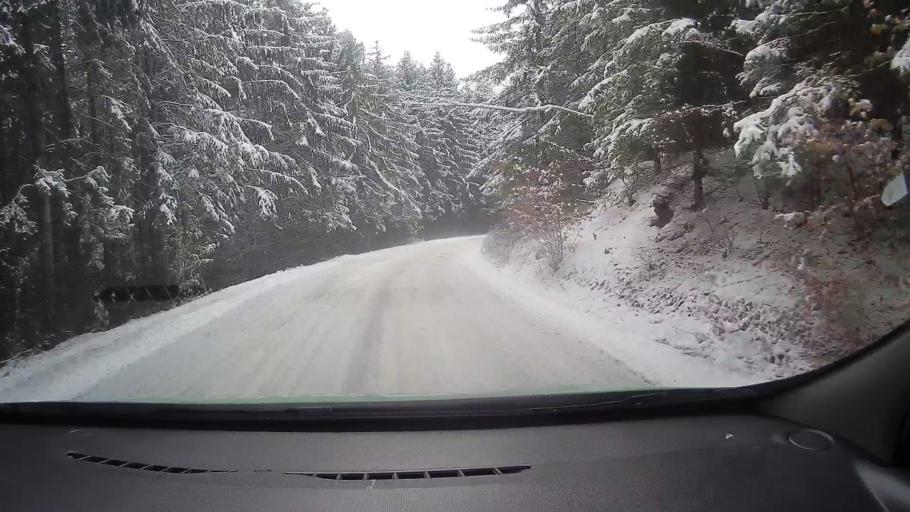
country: RO
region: Alba
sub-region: Comuna Almasu Mare
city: Almasu Mare
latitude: 46.0986
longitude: 23.1532
